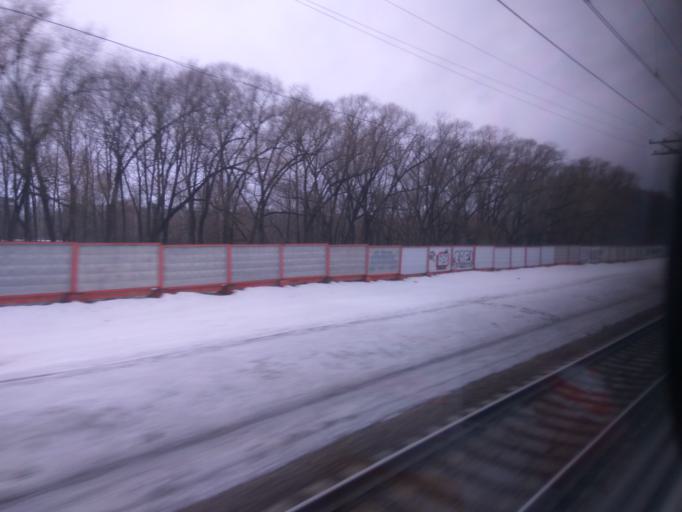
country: RU
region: Tverskaya
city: Tver
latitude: 56.8289
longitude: 35.9091
